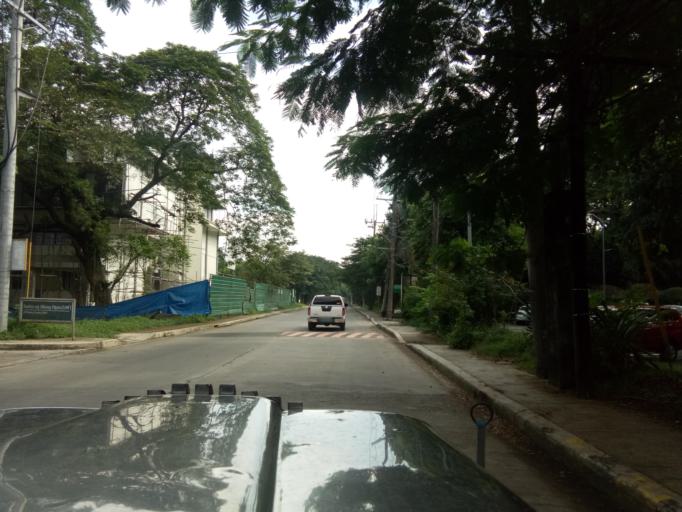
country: PH
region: Metro Manila
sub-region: Quezon City
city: Quezon City
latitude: 14.6571
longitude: 121.0624
